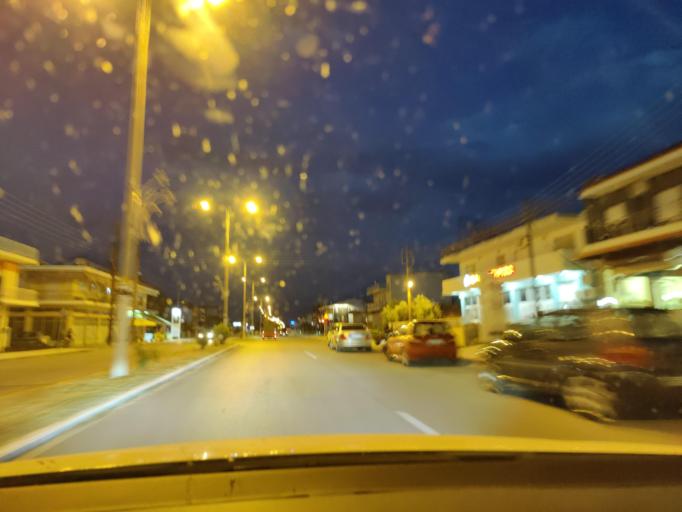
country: GR
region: Central Macedonia
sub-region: Nomos Serron
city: Lefkonas
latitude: 41.0977
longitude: 23.4982
